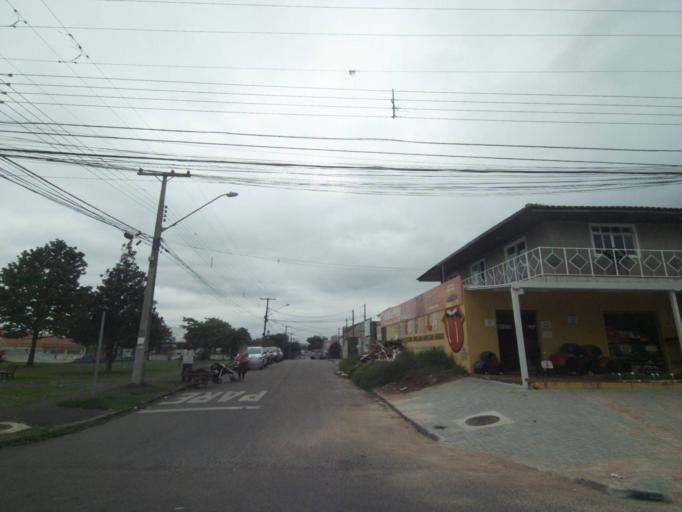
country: BR
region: Parana
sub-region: Sao Jose Dos Pinhais
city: Sao Jose dos Pinhais
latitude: -25.5441
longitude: -49.2583
